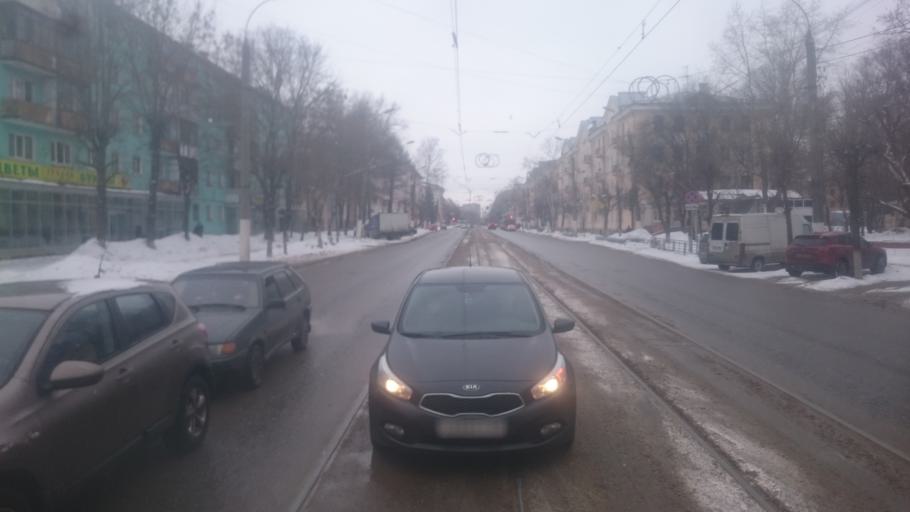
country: RU
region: Tverskaya
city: Tver
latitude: 56.8673
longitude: 35.9057
